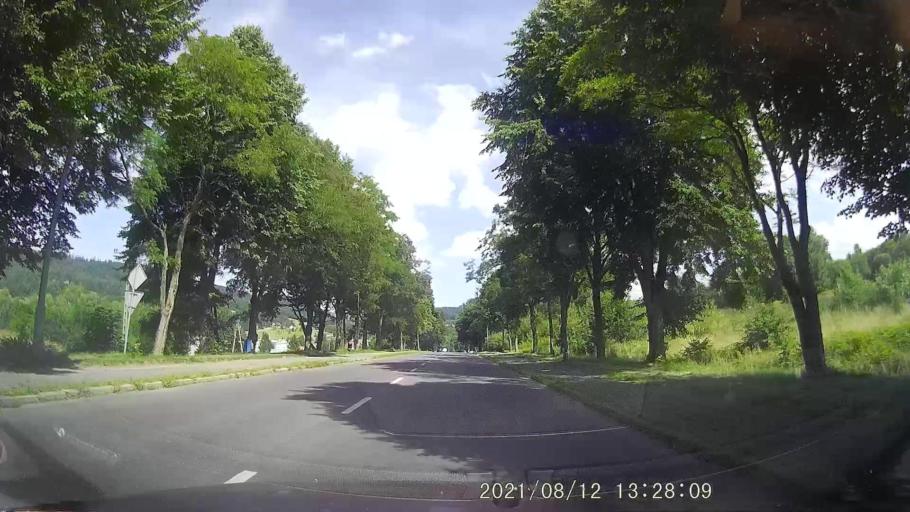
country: PL
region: Lower Silesian Voivodeship
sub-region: Powiat klodzki
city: Ladek-Zdroj
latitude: 50.3408
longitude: 16.8734
